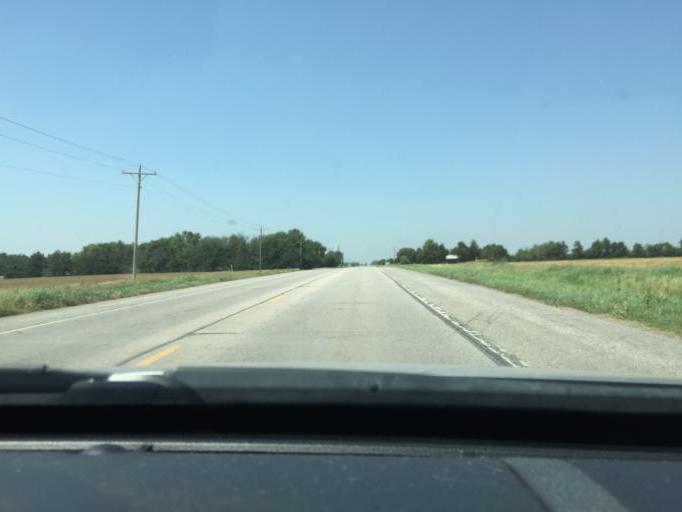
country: US
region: Kansas
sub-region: Reno County
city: Haven
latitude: 37.9455
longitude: -97.8668
